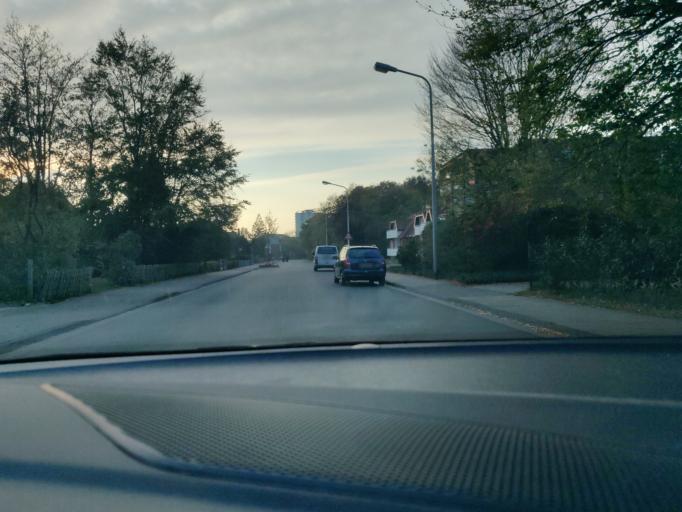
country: DE
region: Lower Saxony
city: Nordholz
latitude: 53.8615
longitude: 8.6078
